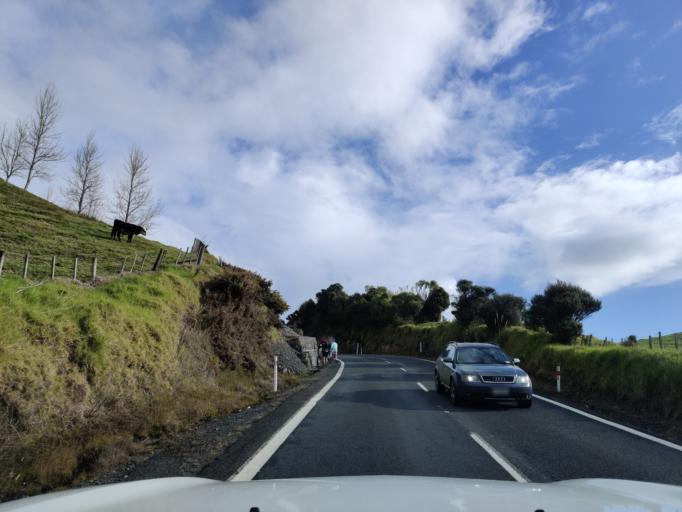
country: NZ
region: Waikato
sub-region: Thames-Coromandel District
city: Coromandel
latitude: -36.8174
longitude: 175.4828
